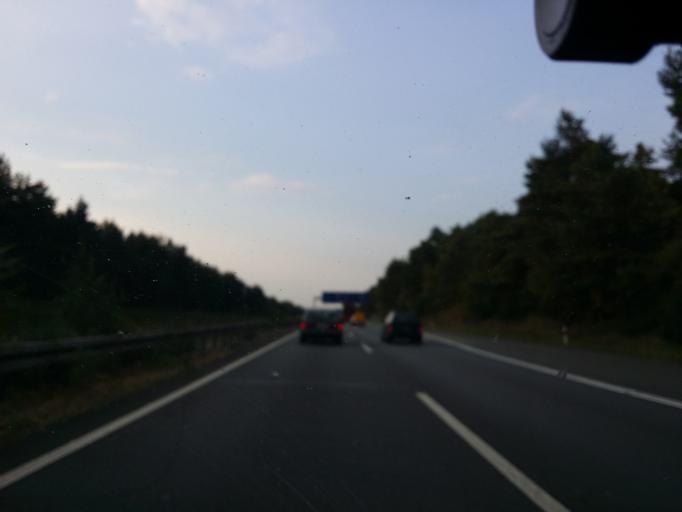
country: DE
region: Hesse
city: Griesheim
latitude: 49.8460
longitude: 8.5955
